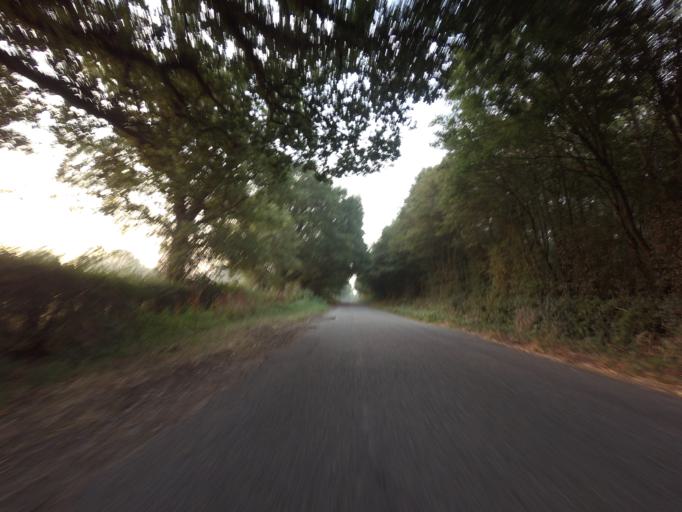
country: GB
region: England
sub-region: Kent
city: Lenham
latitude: 51.1806
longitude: 0.7240
